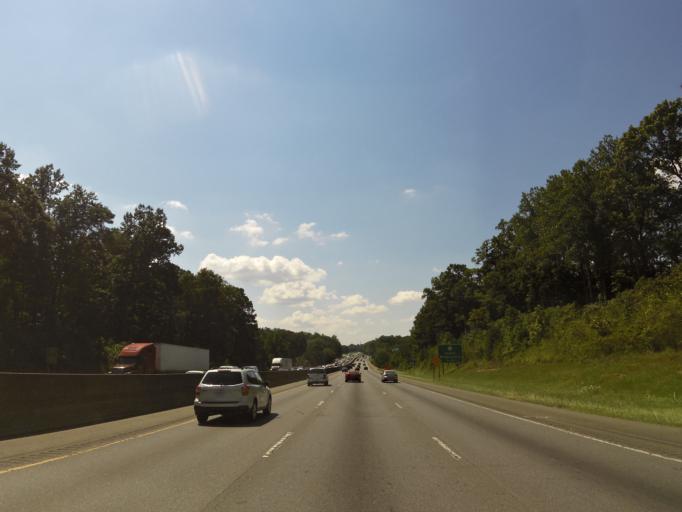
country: US
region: North Carolina
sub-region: Gaston County
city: Cramerton
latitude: 35.2643
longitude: -81.0743
